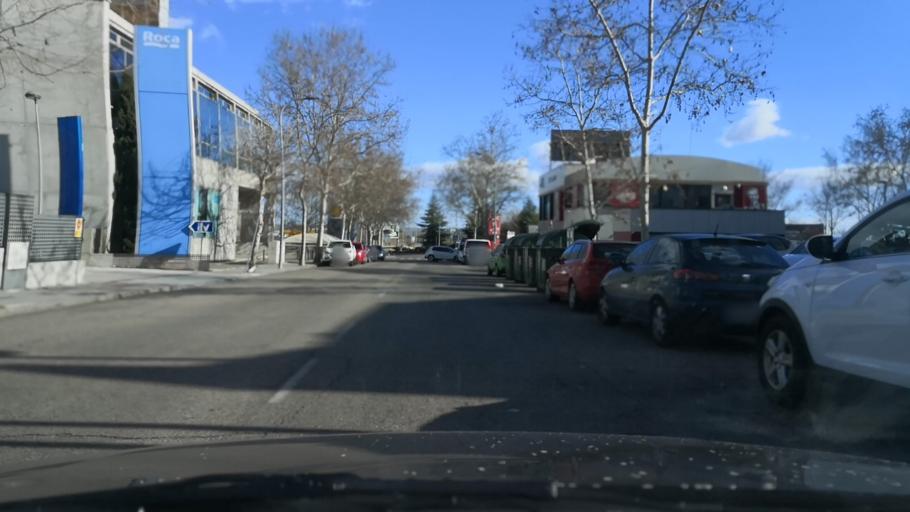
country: ES
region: Madrid
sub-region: Provincia de Madrid
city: San Sebastian de los Reyes
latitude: 40.5476
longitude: -3.6119
